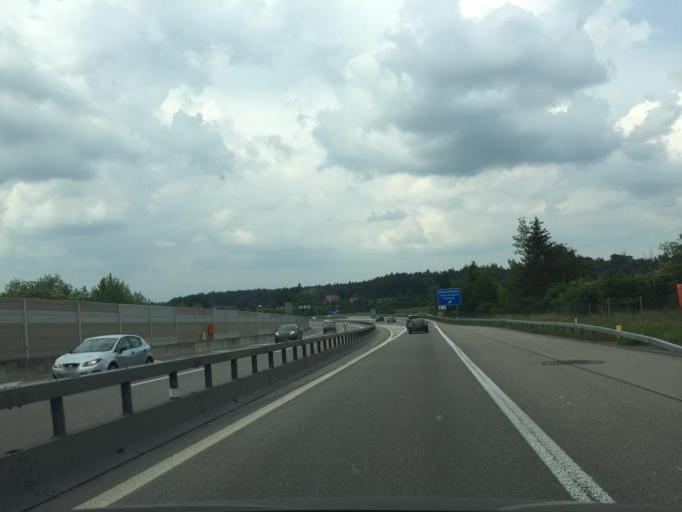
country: CH
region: Zurich
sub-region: Bezirk Andelfingen
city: Kleinandelfingen
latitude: 47.5982
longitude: 8.6910
